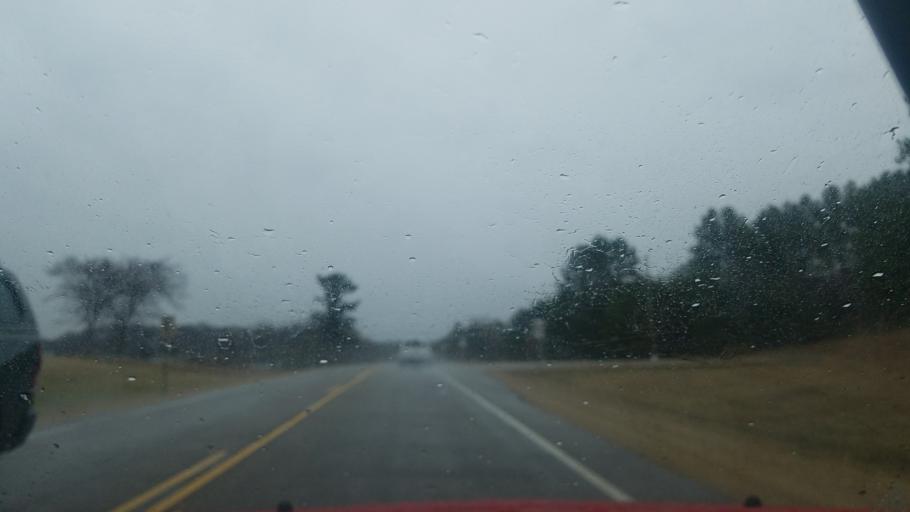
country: US
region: Wisconsin
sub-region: Dunn County
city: Tainter Lake
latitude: 45.0268
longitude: -91.8903
